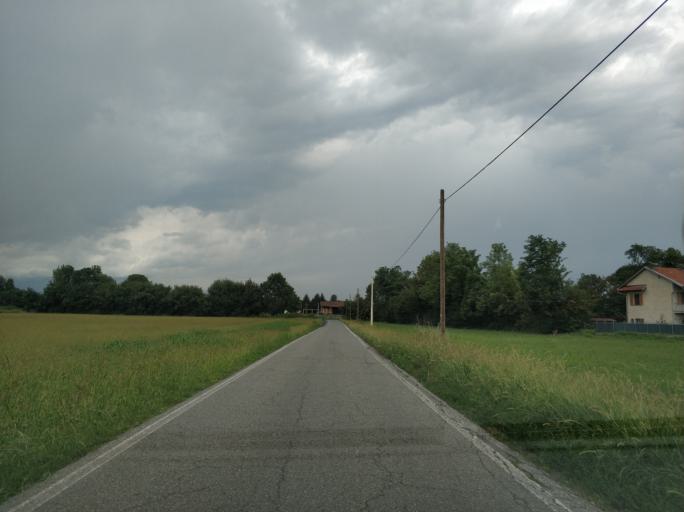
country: IT
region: Piedmont
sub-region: Provincia di Torino
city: Caselle Torinese
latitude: 45.1819
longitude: 7.6252
